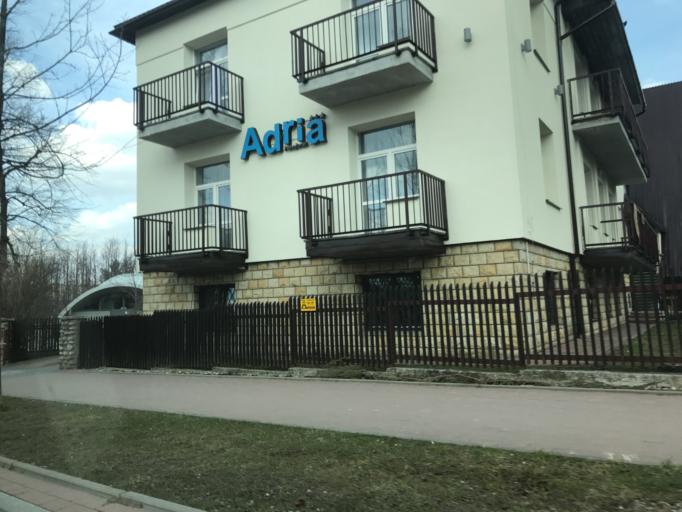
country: PL
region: Lesser Poland Voivodeship
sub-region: Powiat tatrzanski
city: Zakopane
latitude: 49.2901
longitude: 19.9548
